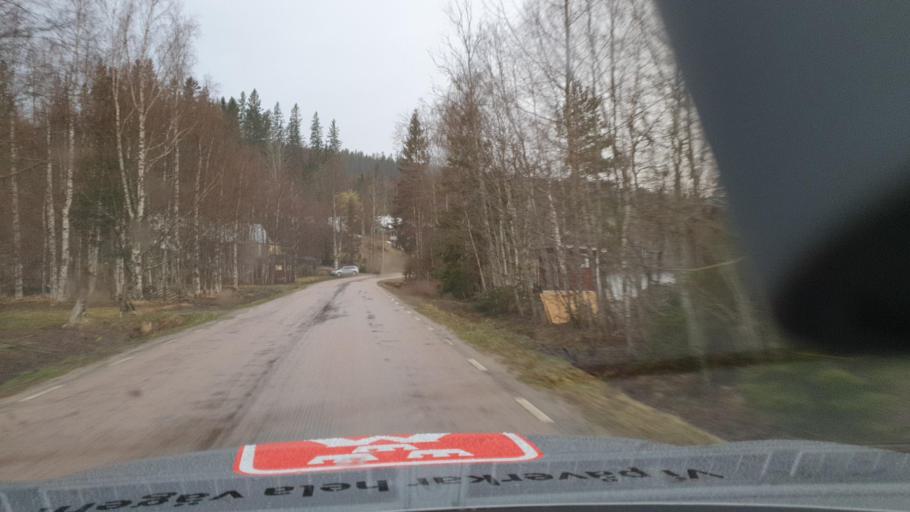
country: SE
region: Vaesternorrland
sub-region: OErnskoeldsviks Kommun
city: Bjasta
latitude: 63.2114
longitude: 18.4178
